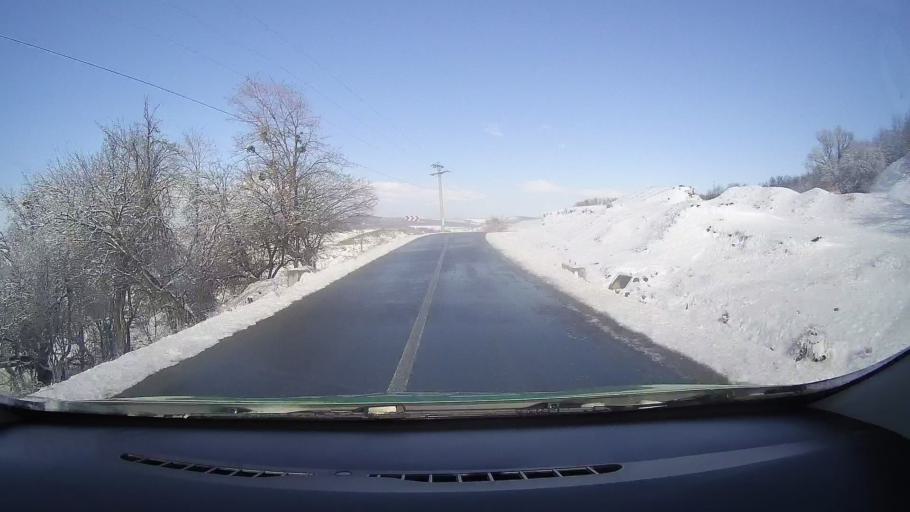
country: RO
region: Sibiu
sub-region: Comuna Rosia
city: Rosia
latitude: 45.7872
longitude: 24.3737
